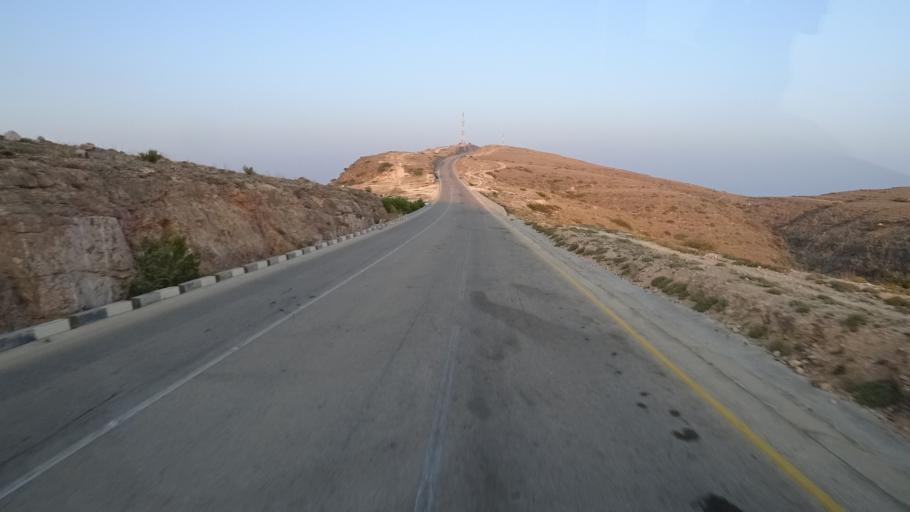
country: OM
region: Zufar
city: Salalah
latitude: 16.8210
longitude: 53.6406
